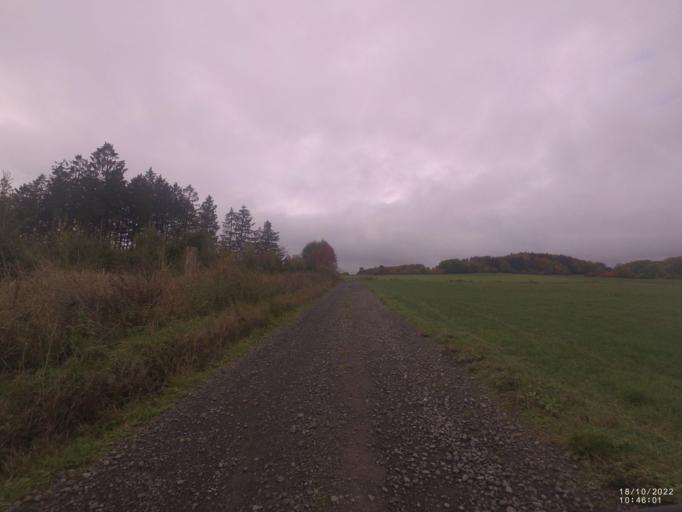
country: DE
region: Rheinland-Pfalz
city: Sarmersbach
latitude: 50.2293
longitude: 6.8998
